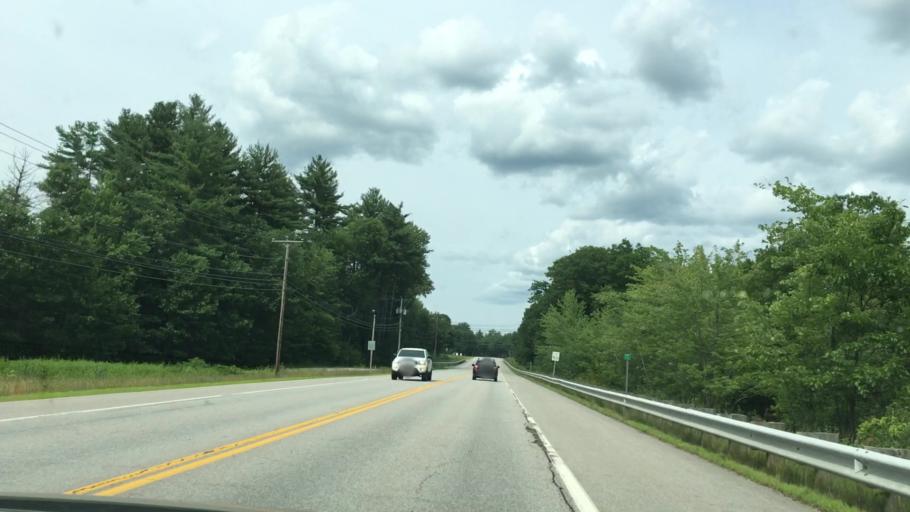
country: US
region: New Hampshire
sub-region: Hillsborough County
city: Peterborough
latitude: 42.8405
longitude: -71.9682
